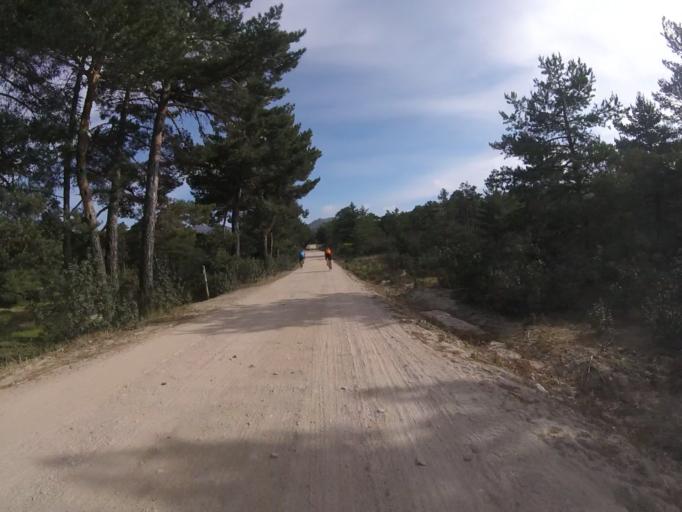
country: ES
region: Castille and Leon
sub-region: Provincia de Avila
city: Peguerinos
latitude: 40.6458
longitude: -4.1784
